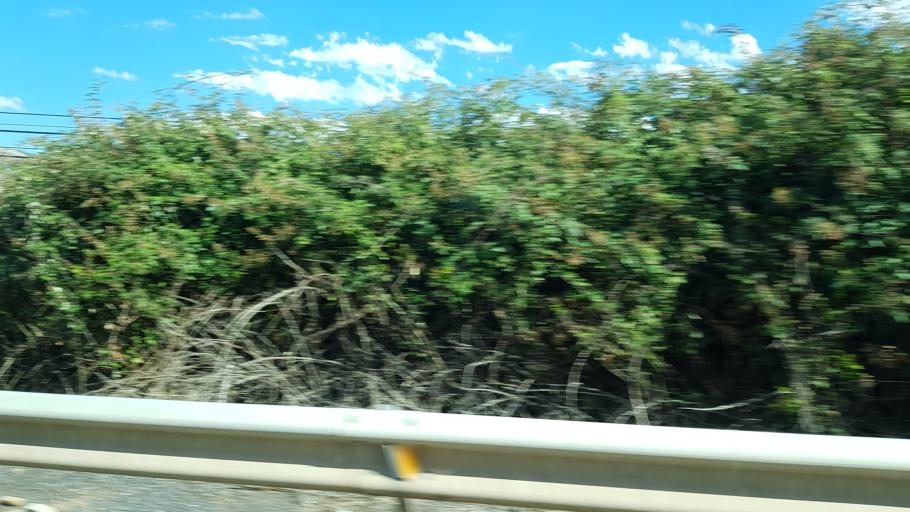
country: ES
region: La Rioja
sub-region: Provincia de La Rioja
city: Sorzano
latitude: 42.3285
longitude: -2.5110
